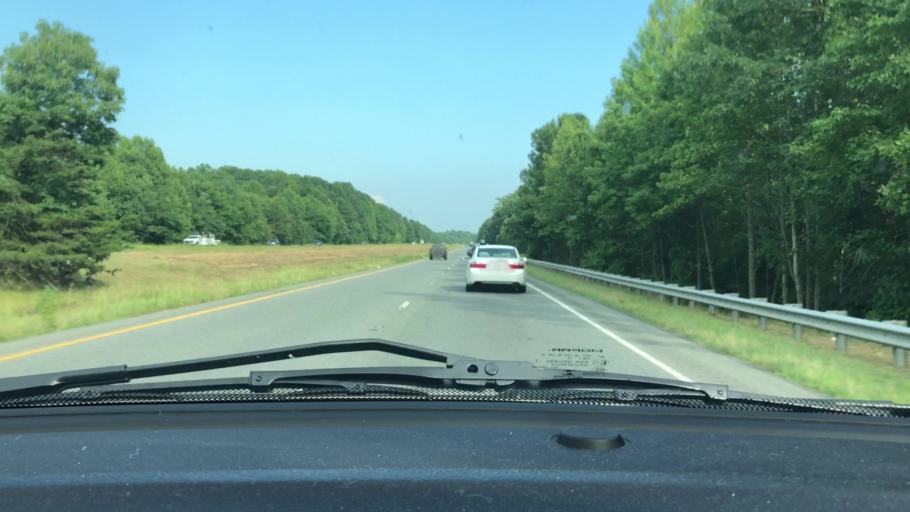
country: US
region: North Carolina
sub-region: Randolph County
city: Liberty
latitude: 35.8934
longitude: -79.6548
